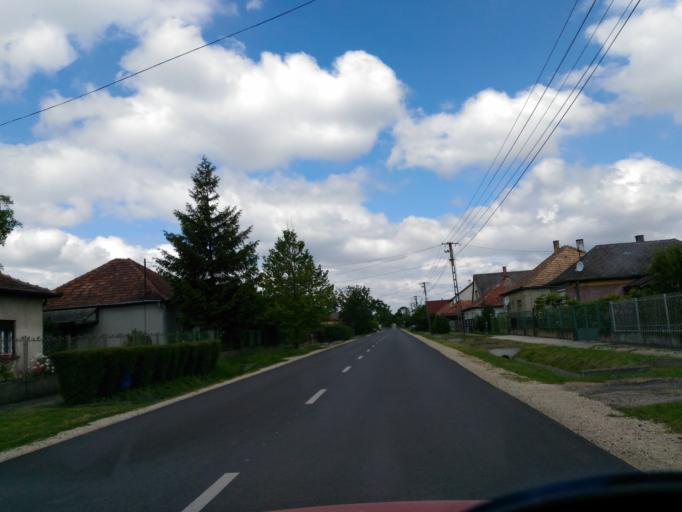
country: HU
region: Fejer
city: Pusztaszabolcs
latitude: 47.1485
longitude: 18.7484
